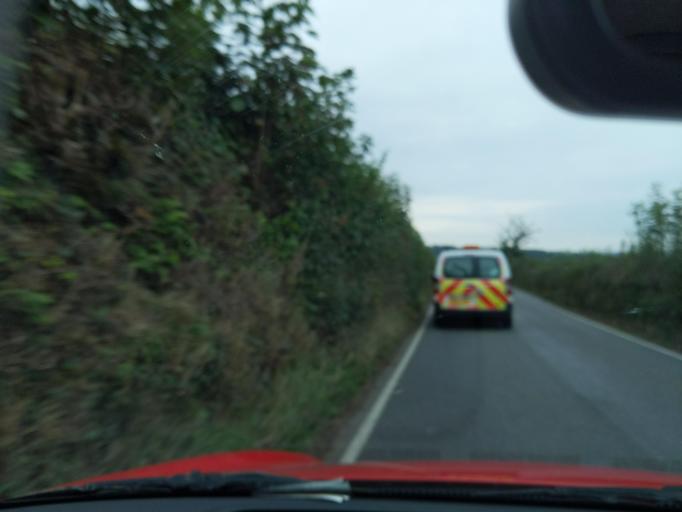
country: GB
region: England
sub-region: Devon
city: Great Torrington
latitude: 50.8672
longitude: -4.0709
